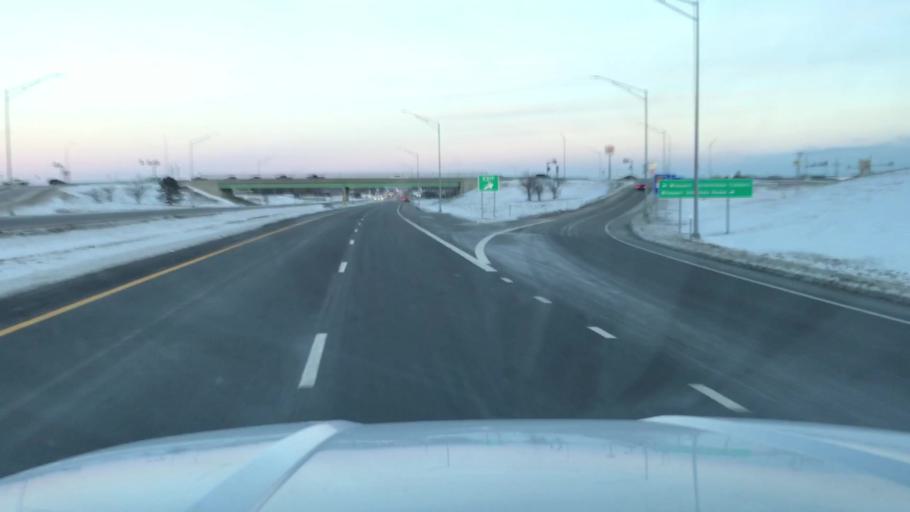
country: US
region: Missouri
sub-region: Clinton County
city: Cameron
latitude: 39.7544
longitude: -94.2373
